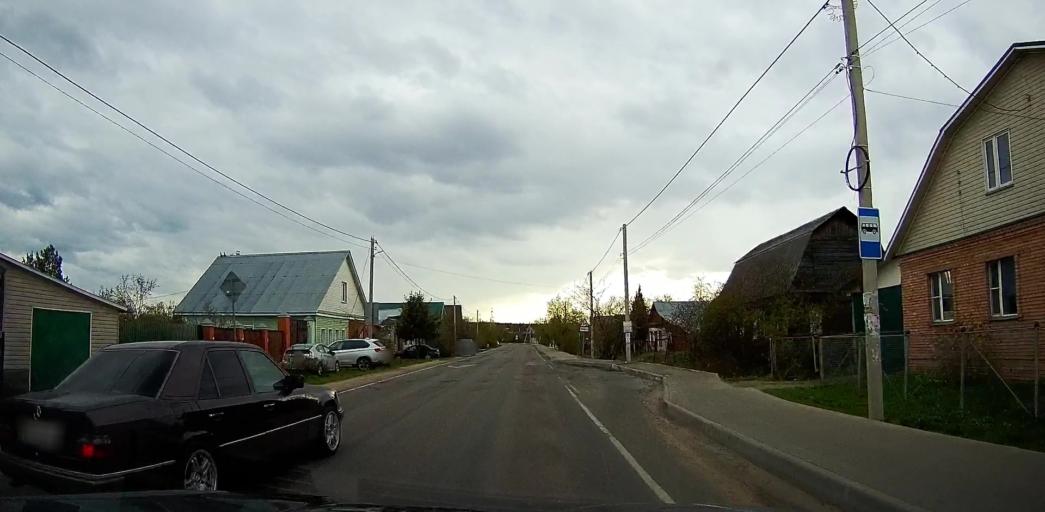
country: RU
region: Moskovskaya
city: Pavlovskiy Posad
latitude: 55.7541
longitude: 38.7031
